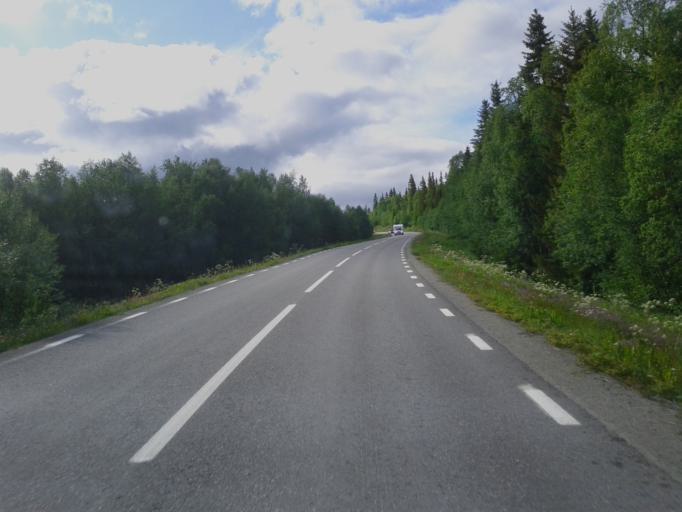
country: NO
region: Nordland
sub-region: Rana
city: Mo i Rana
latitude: 65.7105
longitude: 15.2322
